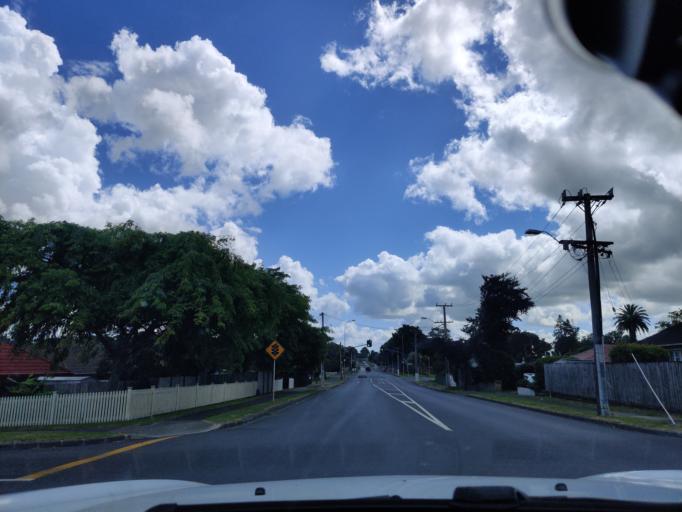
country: NZ
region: Auckland
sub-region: Auckland
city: Papakura
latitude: -37.0692
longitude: 174.9475
